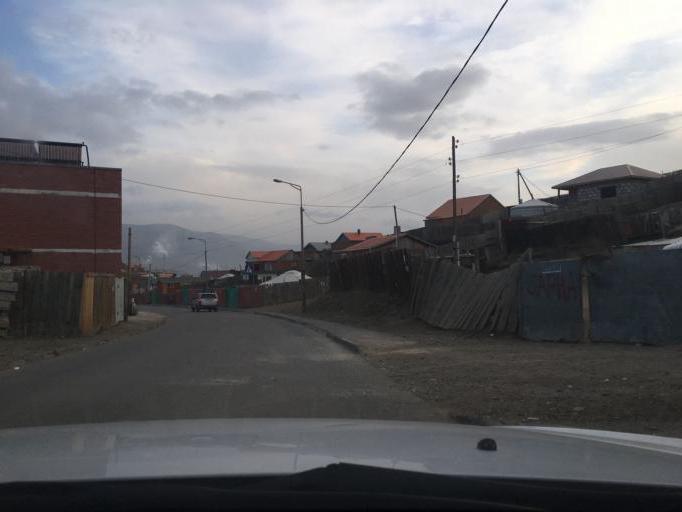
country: MN
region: Ulaanbaatar
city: Ulaanbaatar
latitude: 47.9307
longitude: 106.8582
